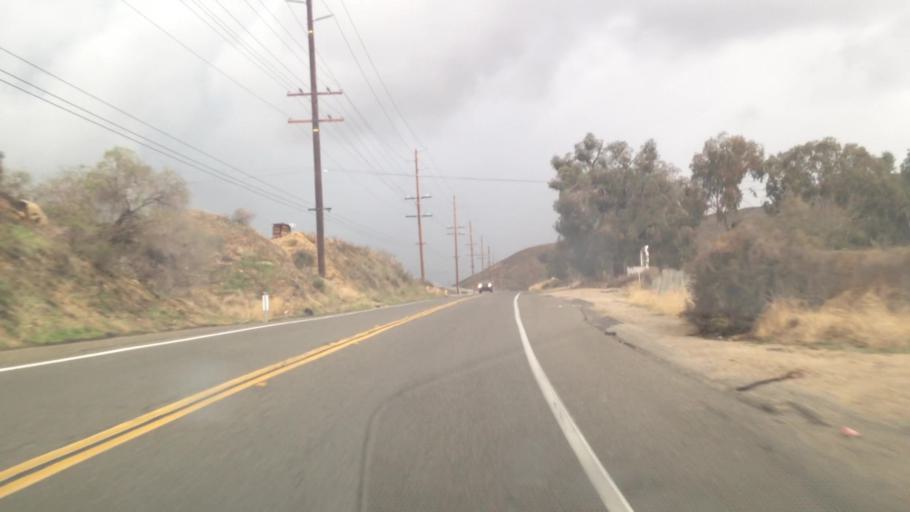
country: US
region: California
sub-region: Riverside County
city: El Cerrito
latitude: 33.7444
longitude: -117.4409
